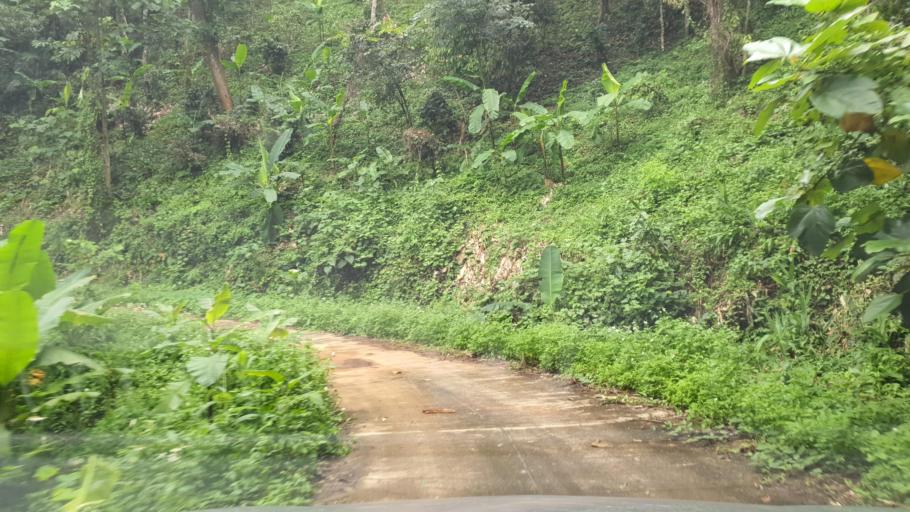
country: TH
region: Chiang Mai
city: Mae On
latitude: 18.9261
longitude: 99.3093
